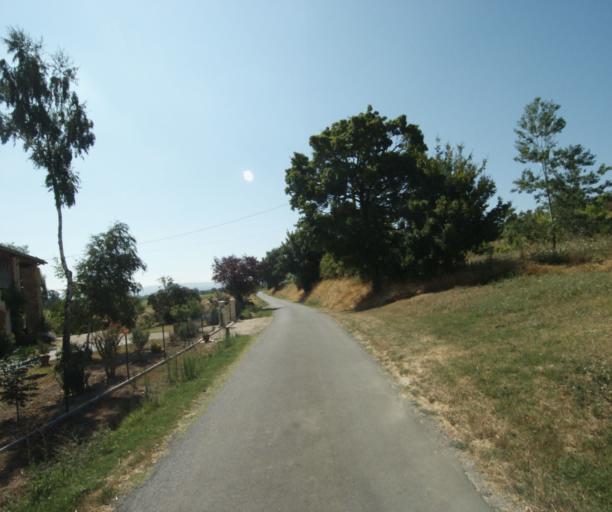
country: FR
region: Midi-Pyrenees
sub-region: Departement de la Haute-Garonne
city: Revel
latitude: 43.5109
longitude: 1.9505
